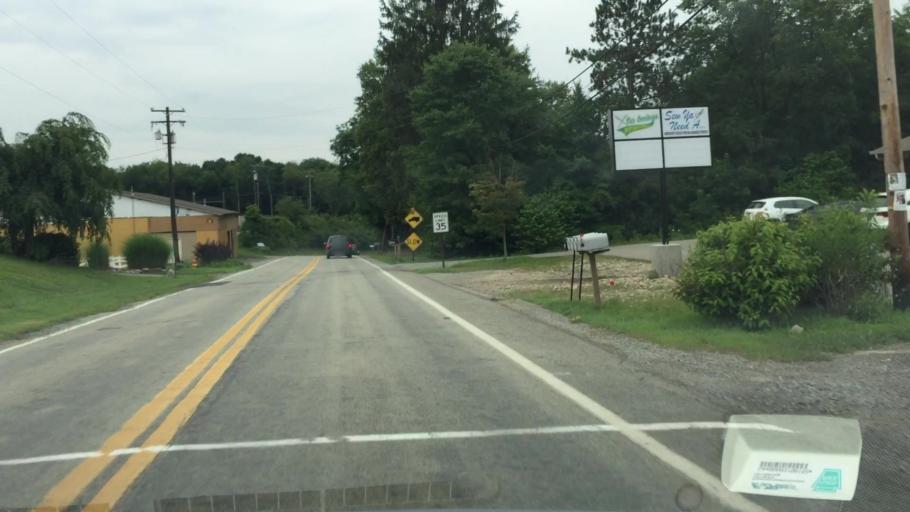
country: US
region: Pennsylvania
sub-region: Allegheny County
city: Curtisville
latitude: 40.6503
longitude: -79.8430
